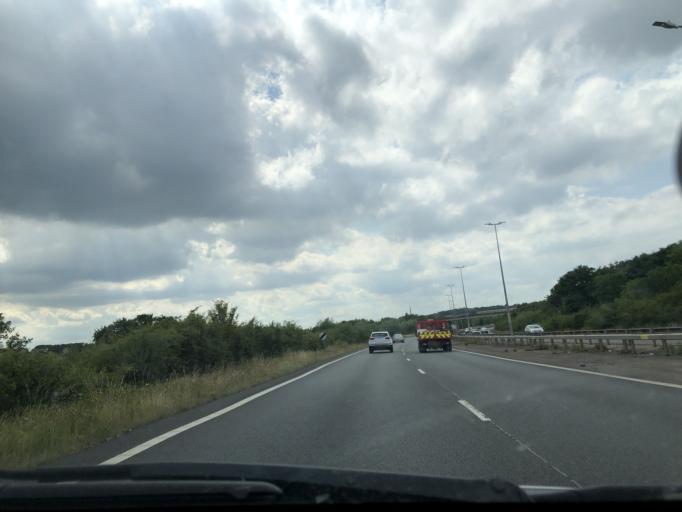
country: GB
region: England
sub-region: Kent
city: Tankerton
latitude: 51.3389
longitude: 1.0544
